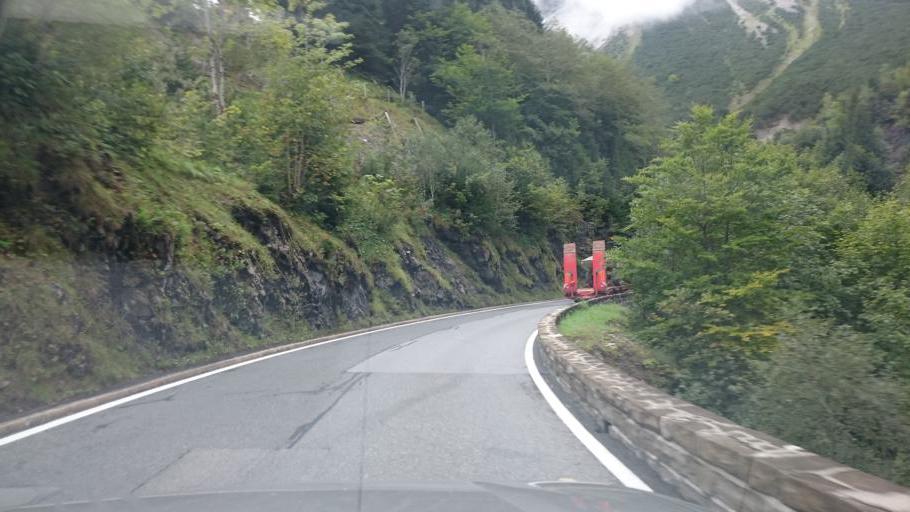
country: AT
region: Vorarlberg
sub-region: Politischer Bezirk Bregenz
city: Schoppernau
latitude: 47.2892
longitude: 10.0459
